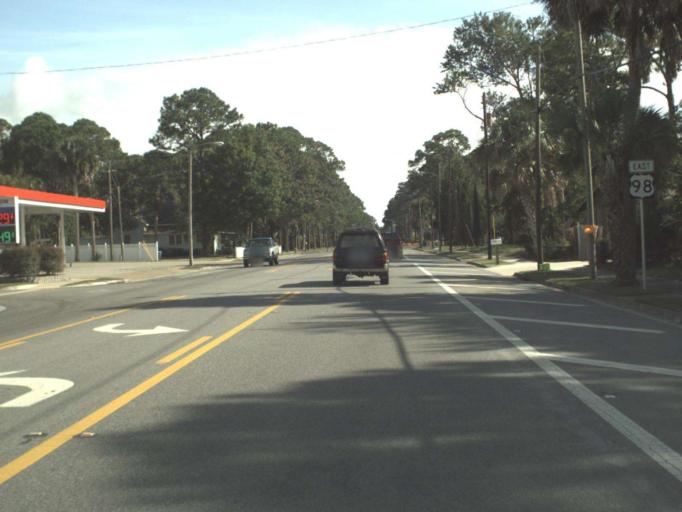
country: US
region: Florida
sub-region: Gulf County
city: Port Saint Joe
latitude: 29.8099
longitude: -85.3027
